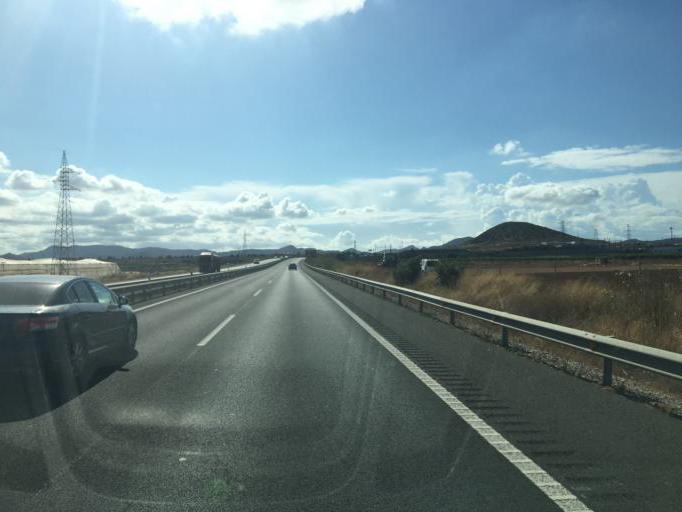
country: ES
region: Murcia
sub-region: Murcia
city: Cartagena
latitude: 37.6424
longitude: -0.9651
